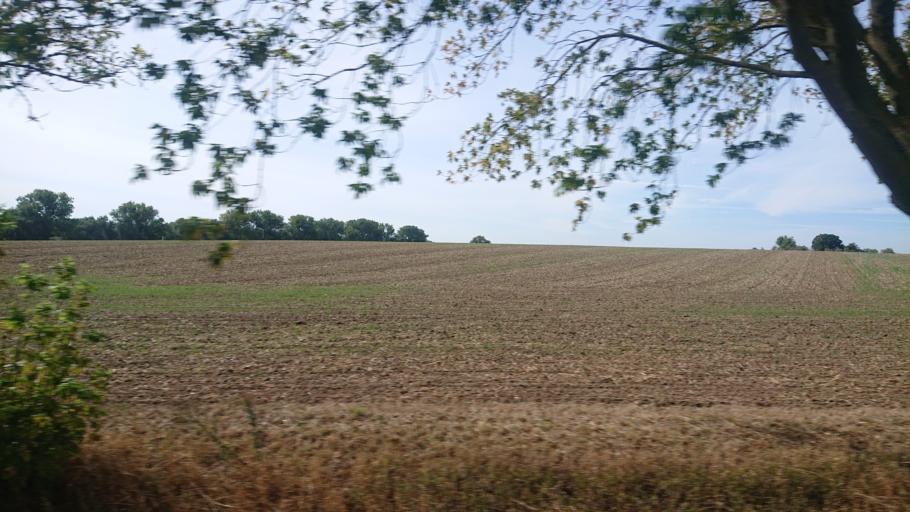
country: DE
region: Brandenburg
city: Grunow
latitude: 53.2818
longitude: 13.9140
